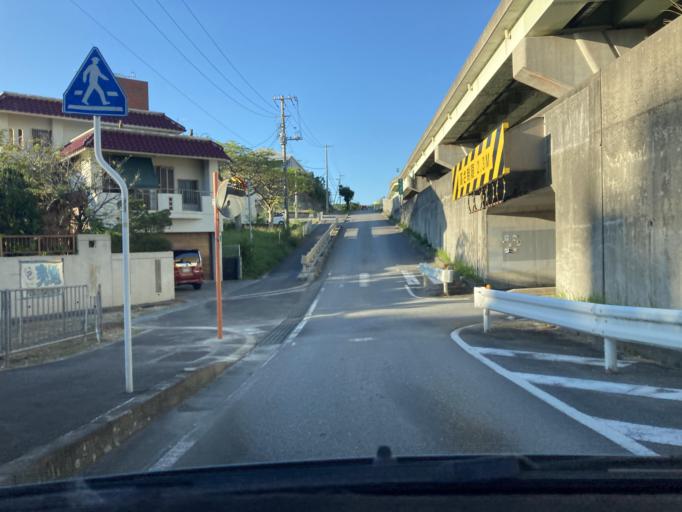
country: JP
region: Okinawa
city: Naha-shi
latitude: 26.2032
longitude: 127.7386
